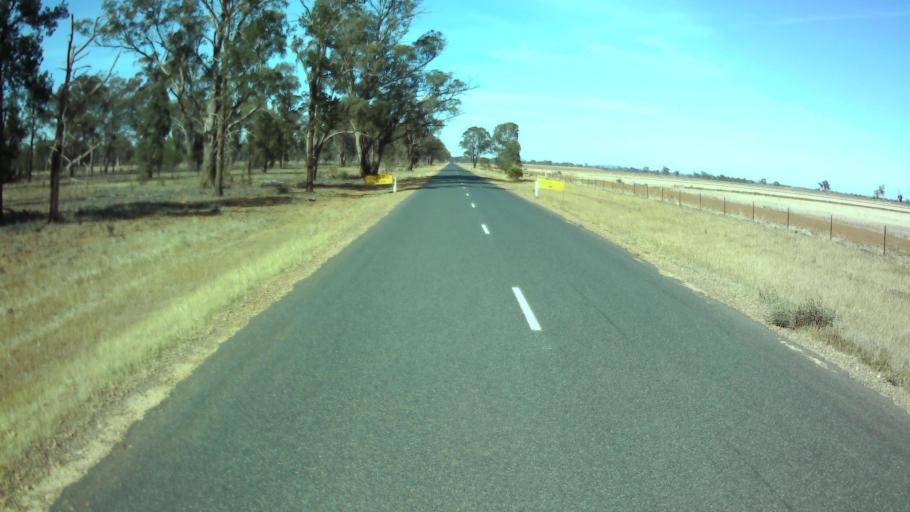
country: AU
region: New South Wales
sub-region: Weddin
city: Grenfell
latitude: -34.1181
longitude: 147.8158
